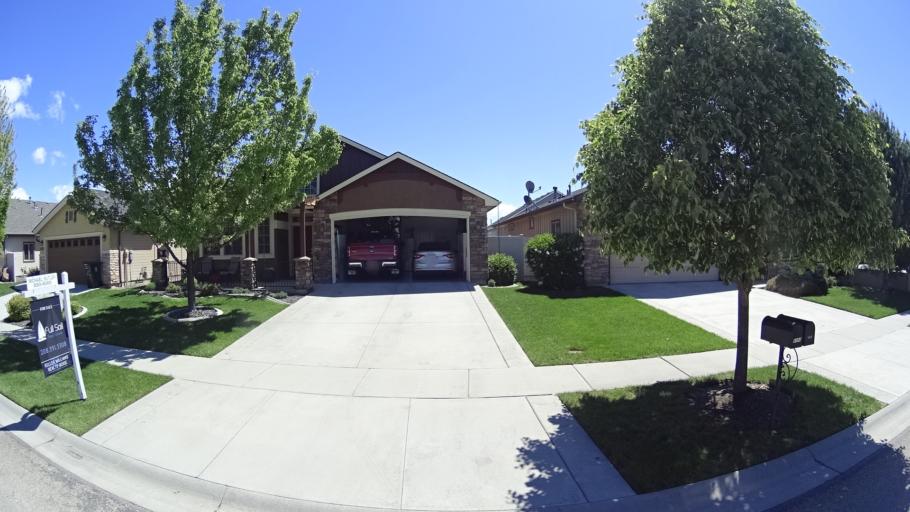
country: US
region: Idaho
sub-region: Ada County
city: Eagle
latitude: 43.6599
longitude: -116.3824
